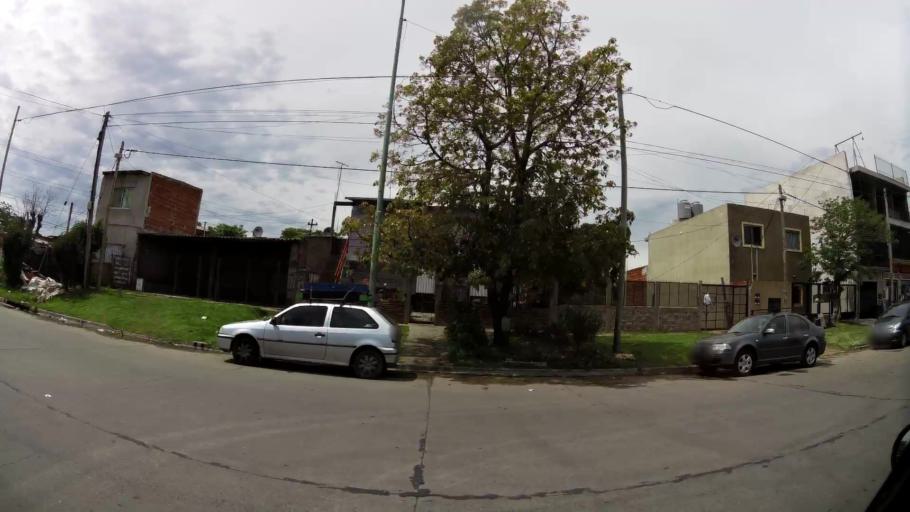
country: AR
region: Buenos Aires
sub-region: Partido de Quilmes
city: Quilmes
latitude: -34.7690
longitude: -58.2334
